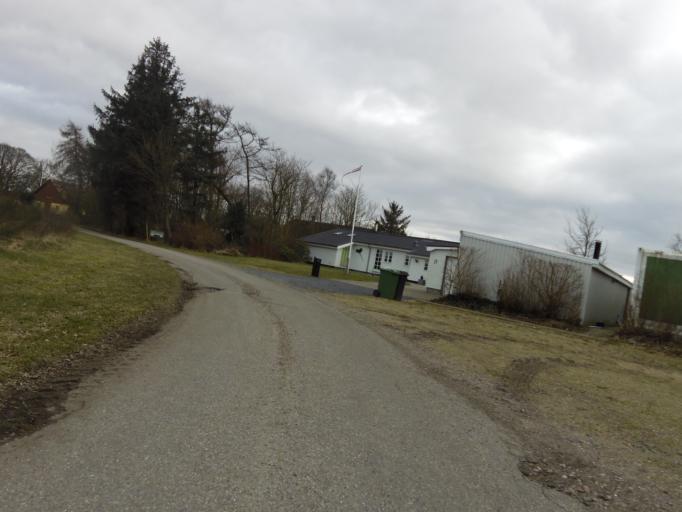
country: DK
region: South Denmark
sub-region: Tonder Kommune
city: Toftlund
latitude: 55.2092
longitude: 9.1737
